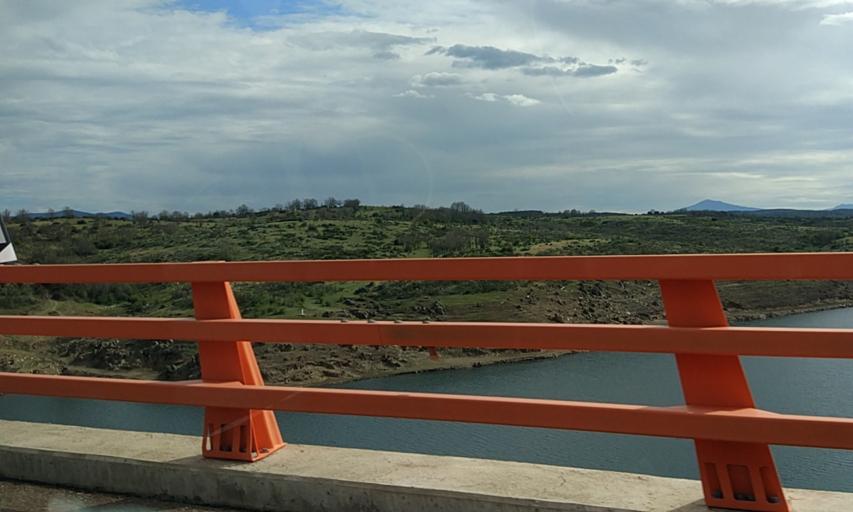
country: ES
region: Castille and Leon
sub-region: Provincia de Salamanca
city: Robleda
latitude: 40.4291
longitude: -6.6032
